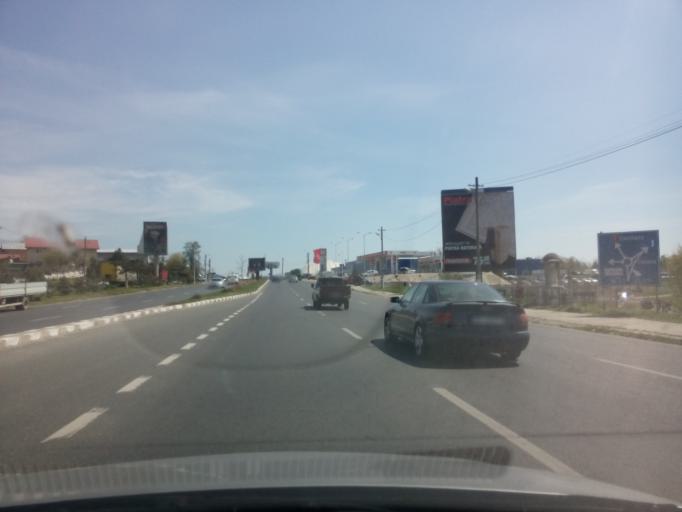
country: RO
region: Ilfov
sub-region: Comuna Pantelimon
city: Pantelimon
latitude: 44.4482
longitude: 26.2067
